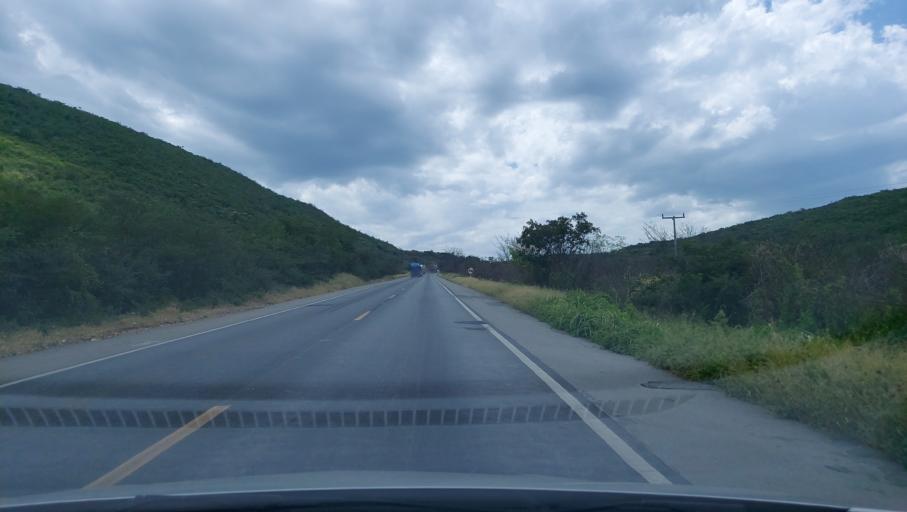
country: BR
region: Bahia
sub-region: Oliveira Dos Brejinhos
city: Beira Rio
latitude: -12.4695
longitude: -42.2936
